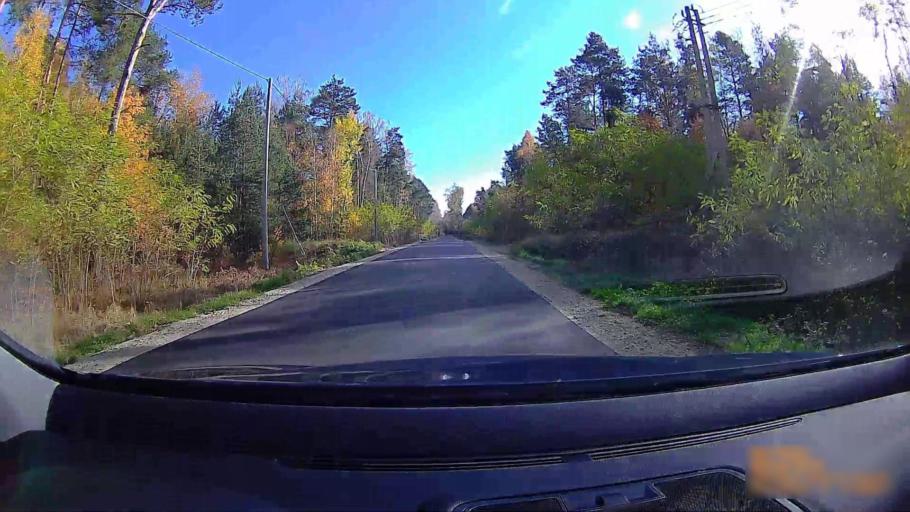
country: PL
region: Greater Poland Voivodeship
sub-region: Powiat ostrzeszowski
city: Ostrzeszow
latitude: 51.4094
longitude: 17.9963
